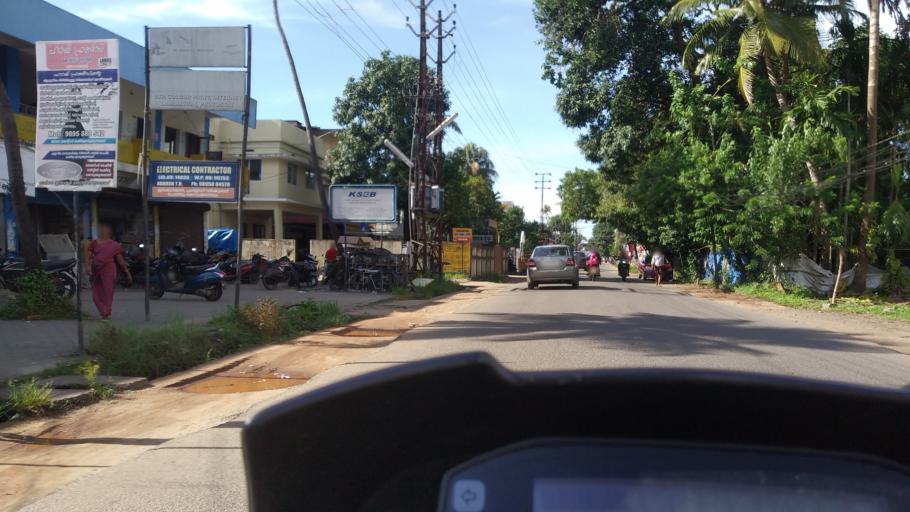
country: IN
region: Kerala
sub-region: Ernakulam
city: Elur
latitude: 10.0436
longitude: 76.2182
